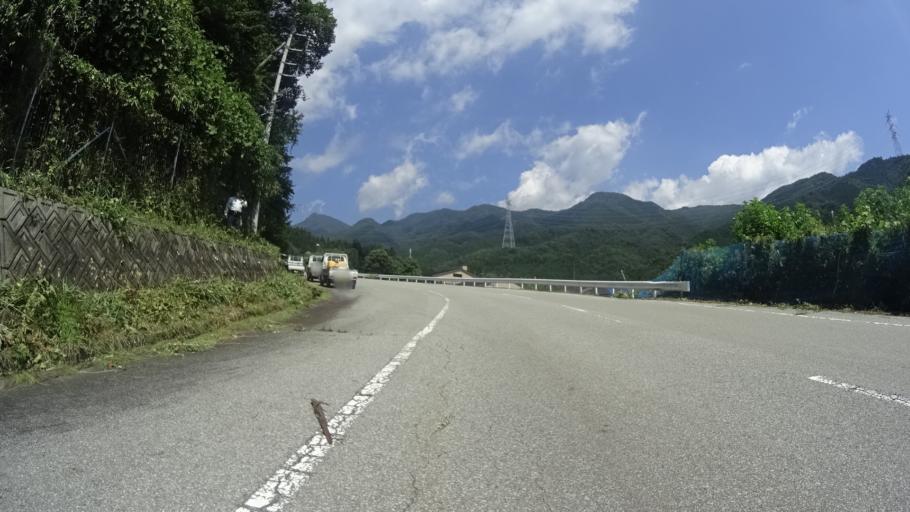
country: JP
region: Yamanashi
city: Enzan
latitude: 35.7737
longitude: 138.6970
